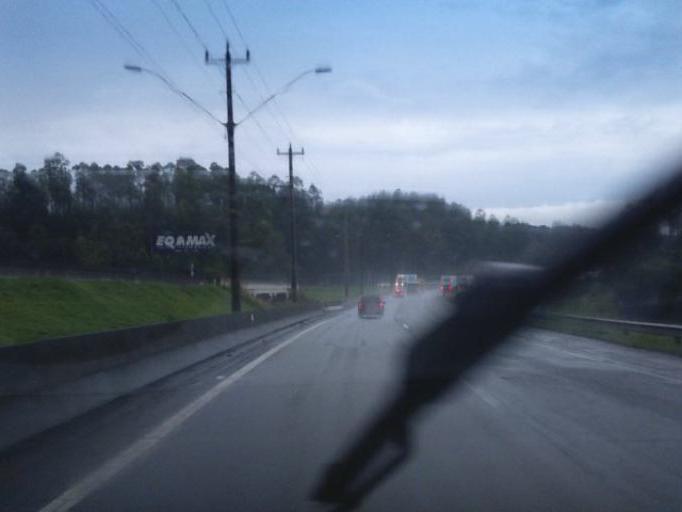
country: BR
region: Sao Paulo
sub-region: Sao Lourenco Da Serra
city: Sao Lourenco da Serra
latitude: -23.7791
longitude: -46.9158
